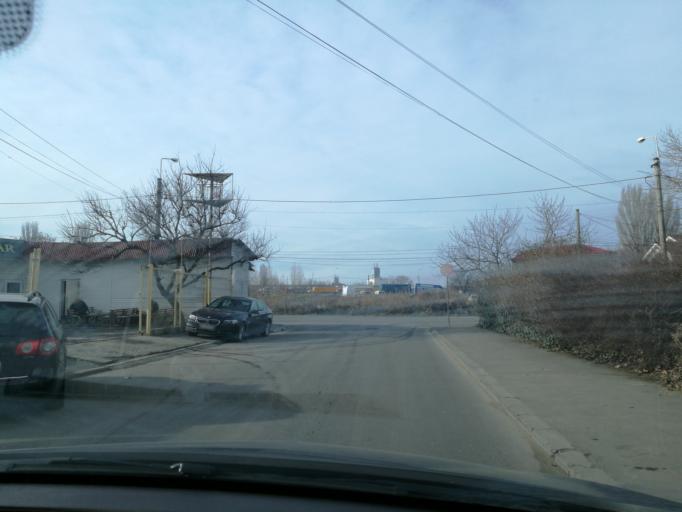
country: RO
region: Constanta
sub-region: Municipiul Constanta
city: Constanta
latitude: 44.1759
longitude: 28.6094
